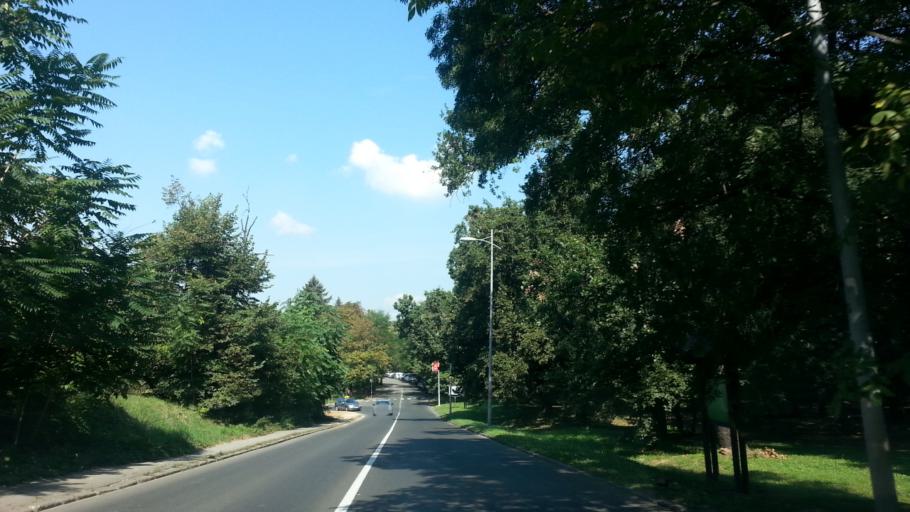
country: RS
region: Central Serbia
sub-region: Belgrade
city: Cukarica
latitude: 44.7626
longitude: 20.4300
